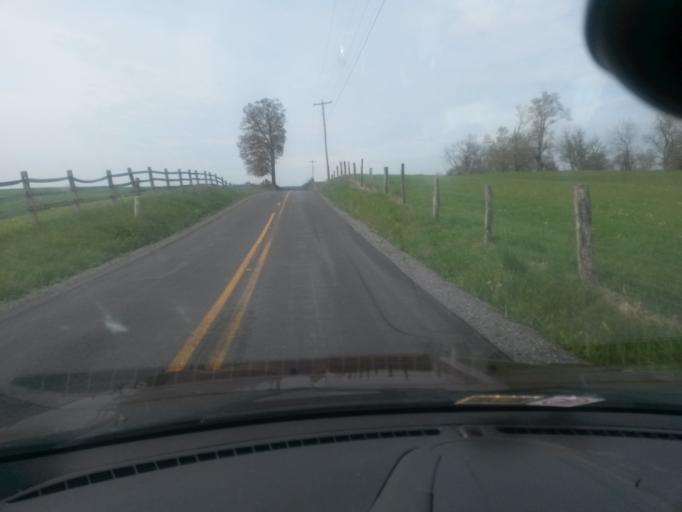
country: US
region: West Virginia
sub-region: Pocahontas County
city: Marlinton
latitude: 38.1135
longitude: -80.2160
